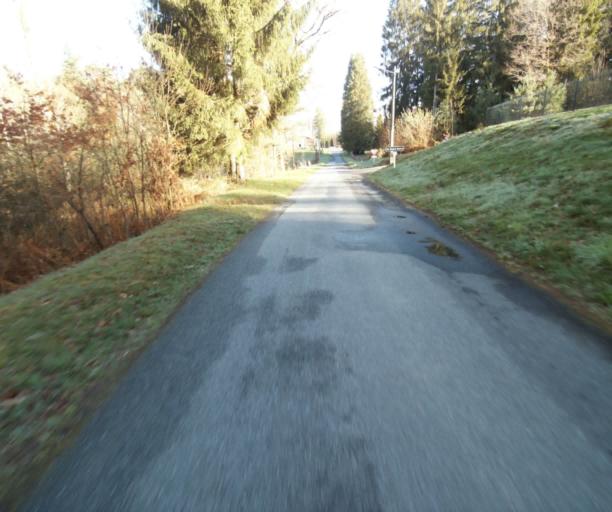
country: FR
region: Limousin
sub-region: Departement de la Correze
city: Correze
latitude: 45.2850
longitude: 1.8659
